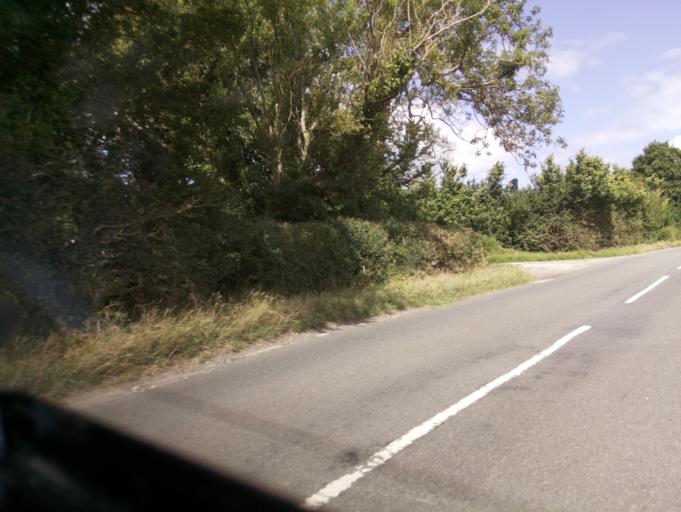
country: GB
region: England
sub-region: Buckinghamshire
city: Winslow
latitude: 51.9322
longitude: -0.8354
